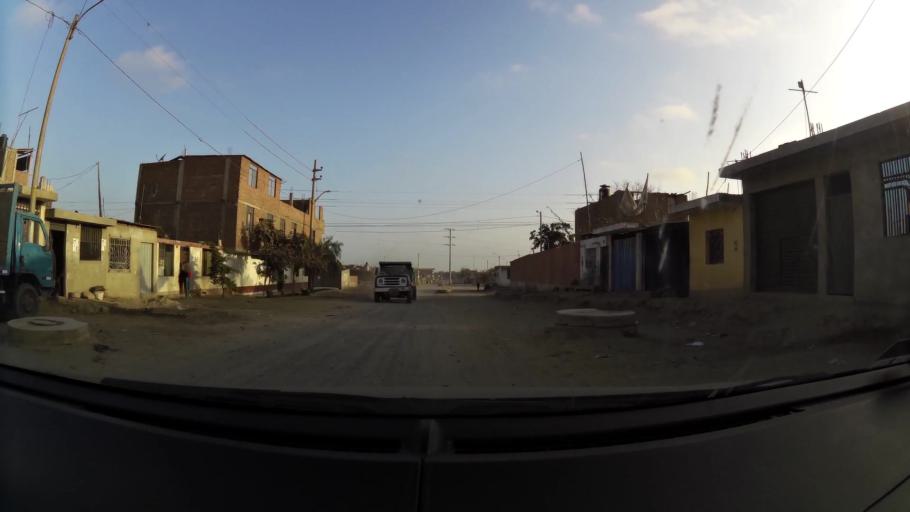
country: PE
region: La Libertad
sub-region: Provincia de Trujillo
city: El Porvenir
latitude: -8.0650
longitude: -78.9951
